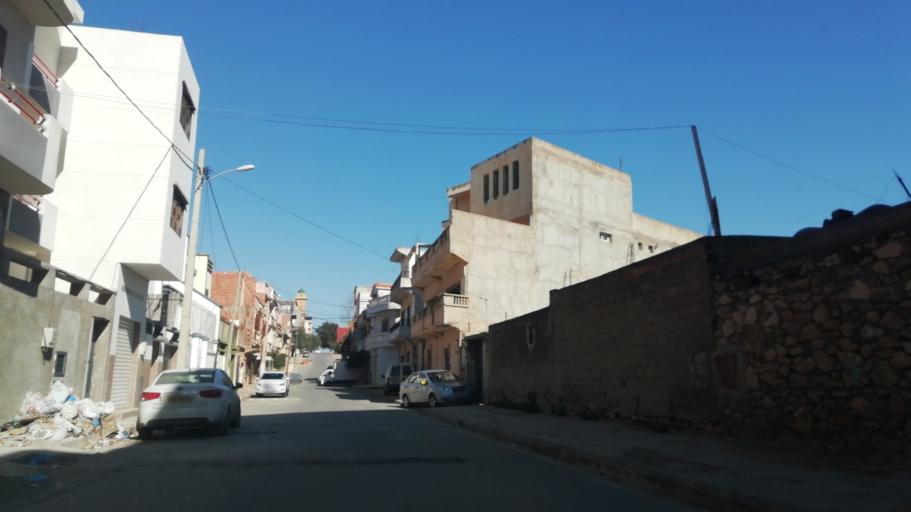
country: DZ
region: Oran
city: Bir el Djir
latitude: 35.7248
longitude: -0.5810
